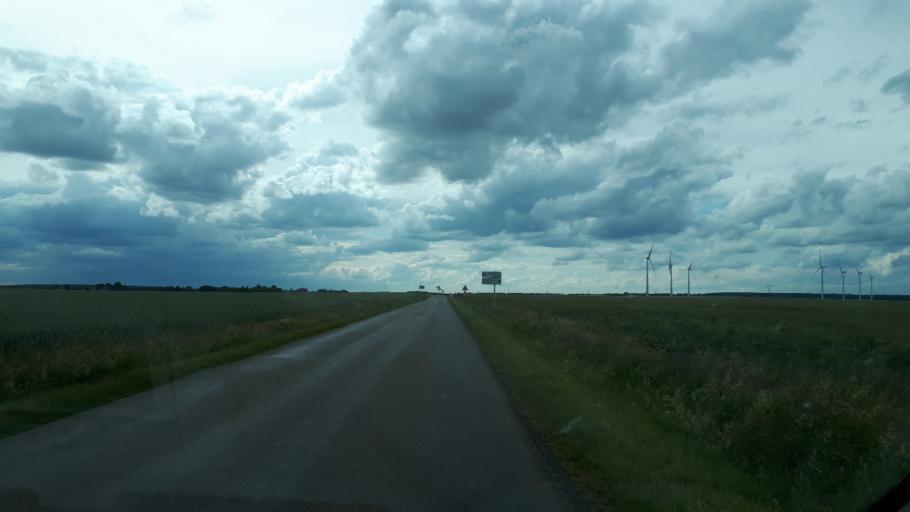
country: FR
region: Centre
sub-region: Departement du Cher
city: Massay
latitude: 47.1011
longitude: 1.9574
